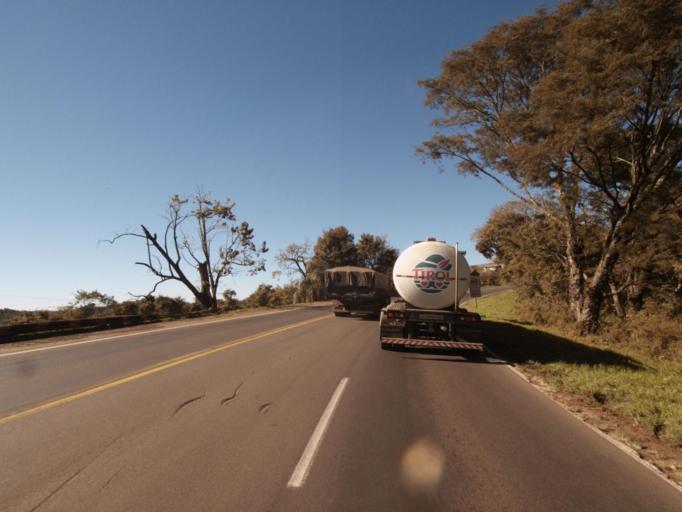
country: BR
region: Santa Catarina
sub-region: Chapeco
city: Chapeco
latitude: -26.9867
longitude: -52.6100
